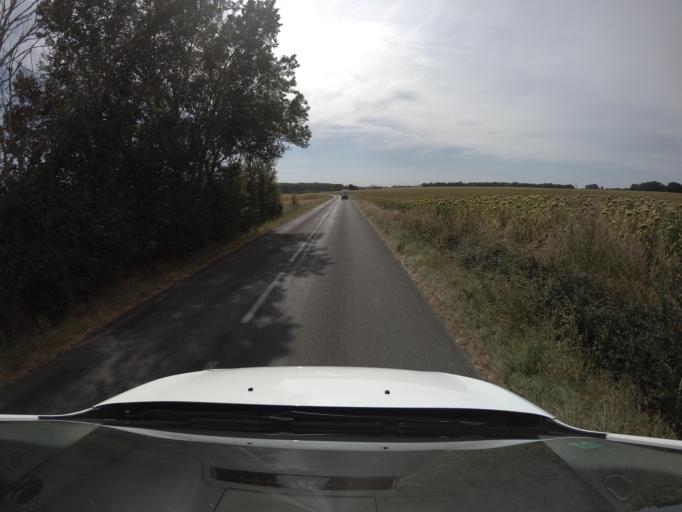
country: FR
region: Poitou-Charentes
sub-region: Departement des Deux-Sevres
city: Saint-Leger-de-Montbrun
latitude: 47.0032
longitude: -0.0879
